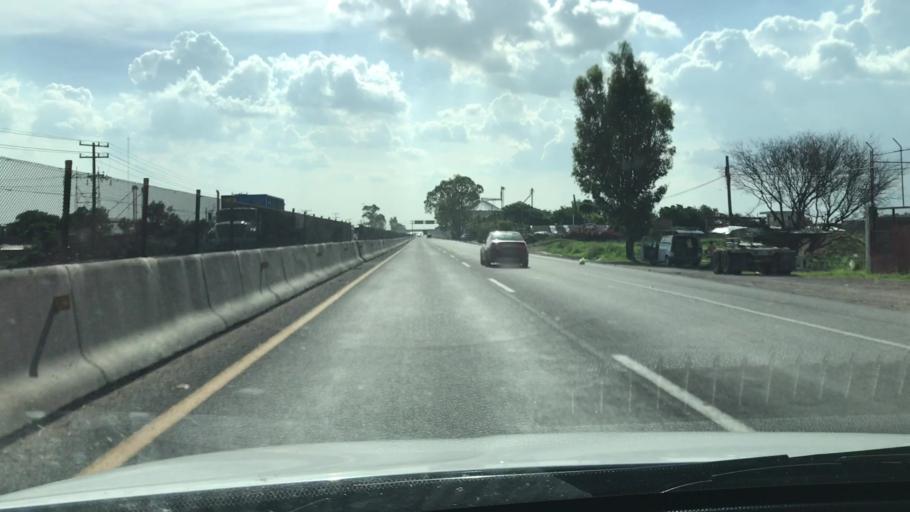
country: MX
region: Guanajuato
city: Villagran
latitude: 20.5098
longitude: -101.0034
